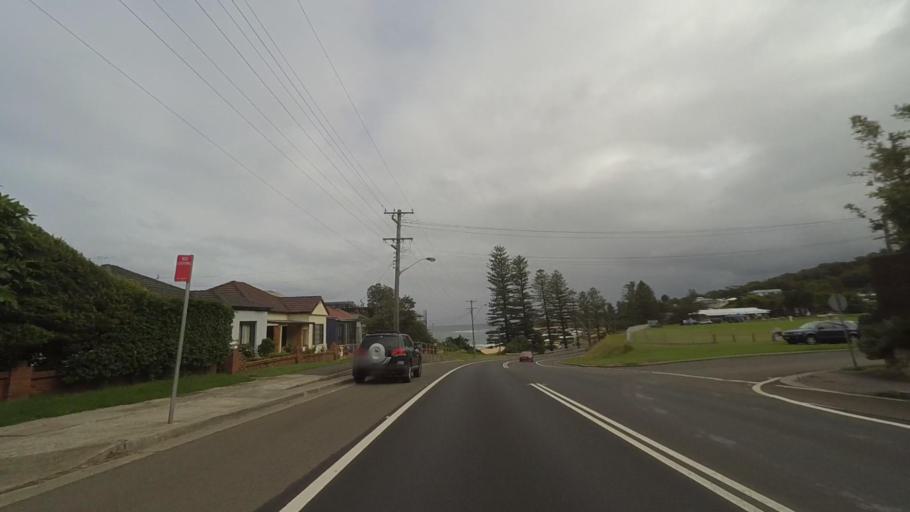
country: AU
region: New South Wales
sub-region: Wollongong
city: Bulli
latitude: -34.2924
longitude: 150.9443
